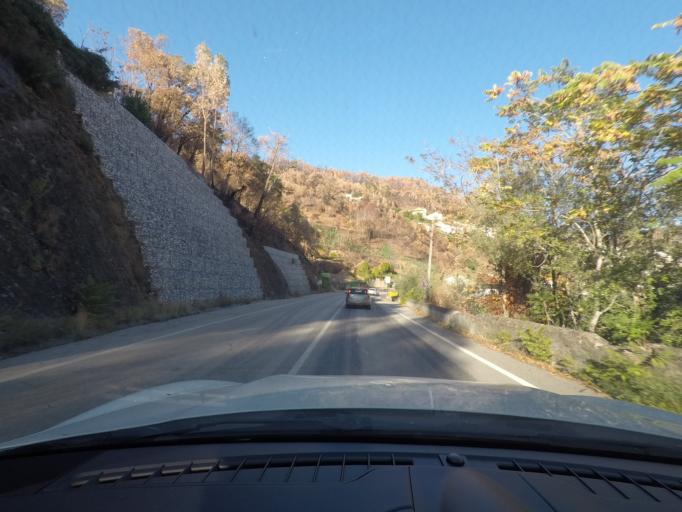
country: PT
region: Coimbra
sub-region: Coimbra
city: Coimbra
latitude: 40.1835
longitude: -8.3591
